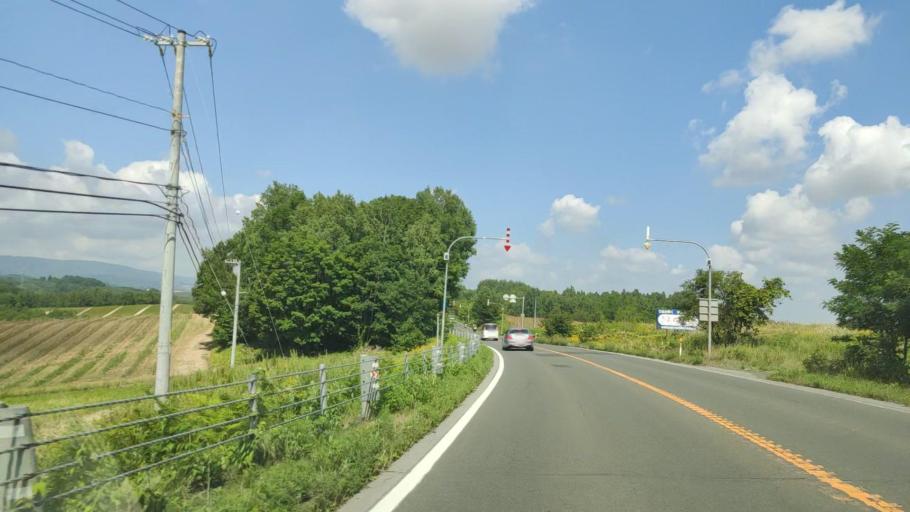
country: JP
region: Hokkaido
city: Shimo-furano
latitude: 43.5063
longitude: 142.4582
